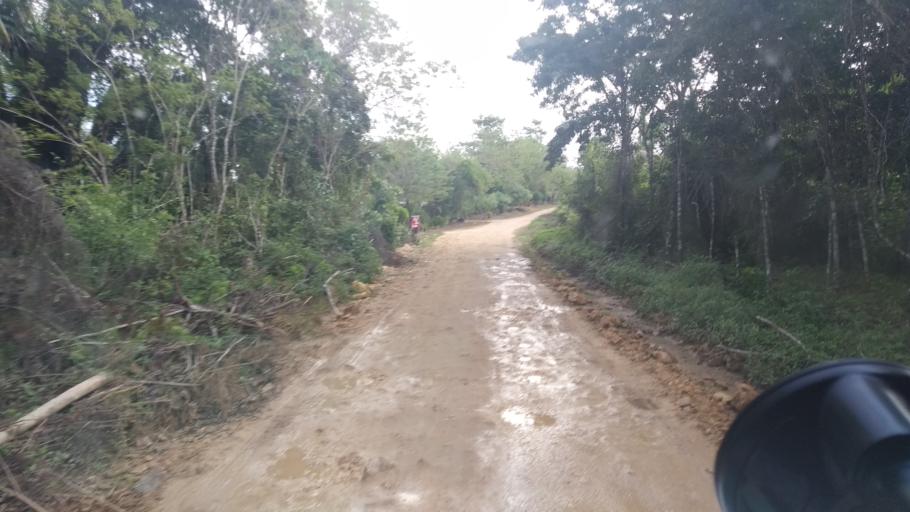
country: BZ
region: Toledo
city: Punta Gorda
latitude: 16.2069
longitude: -88.9184
